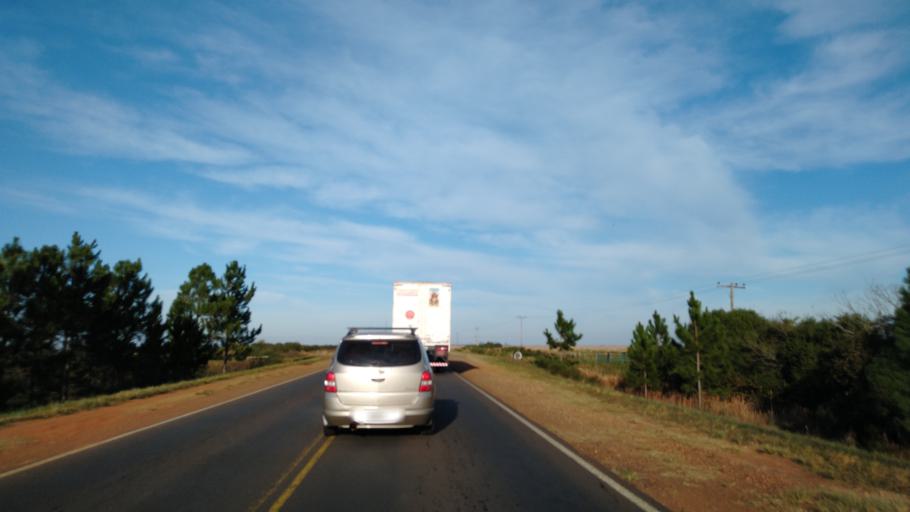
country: AR
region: Corrientes
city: La Cruz
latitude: -29.2091
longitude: -56.6999
